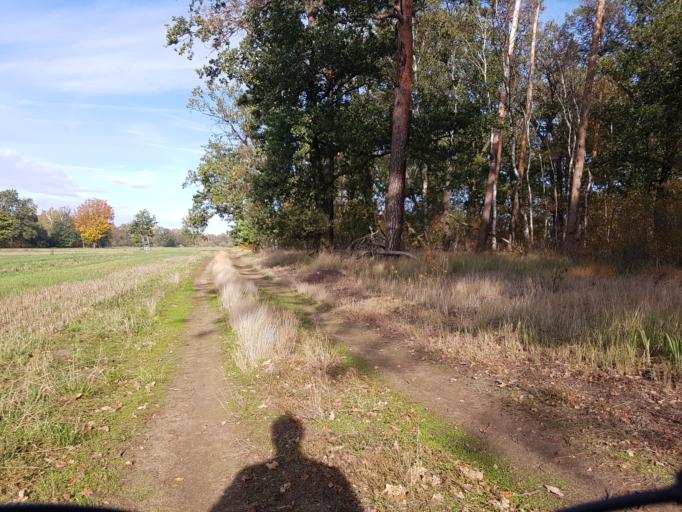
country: DE
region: Brandenburg
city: Schilda
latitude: 51.5956
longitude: 13.3324
